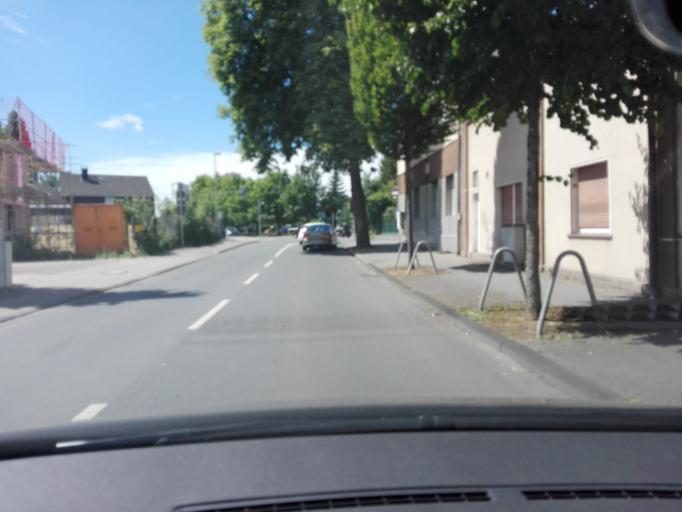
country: DE
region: North Rhine-Westphalia
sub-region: Regierungsbezirk Arnsberg
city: Unna
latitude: 51.5542
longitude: 7.6855
